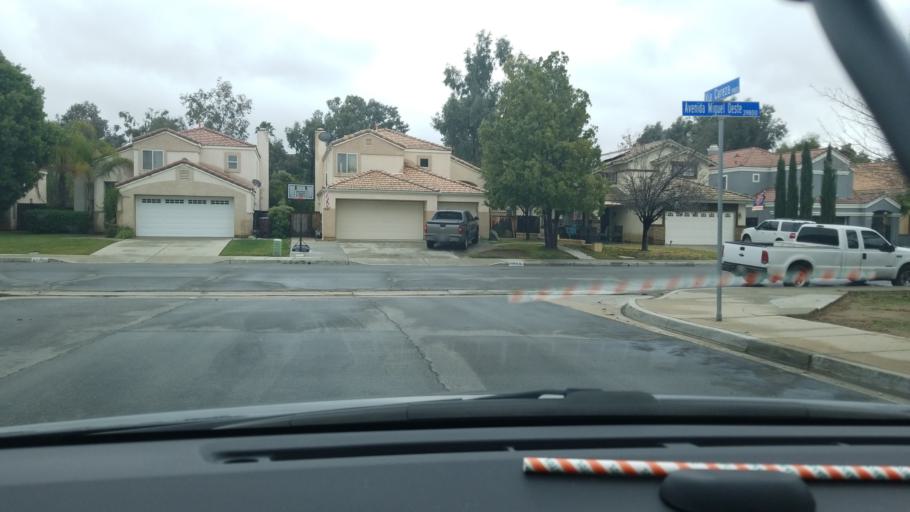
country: US
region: California
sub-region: Riverside County
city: Murrieta Hot Springs
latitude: 33.5676
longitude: -117.1775
